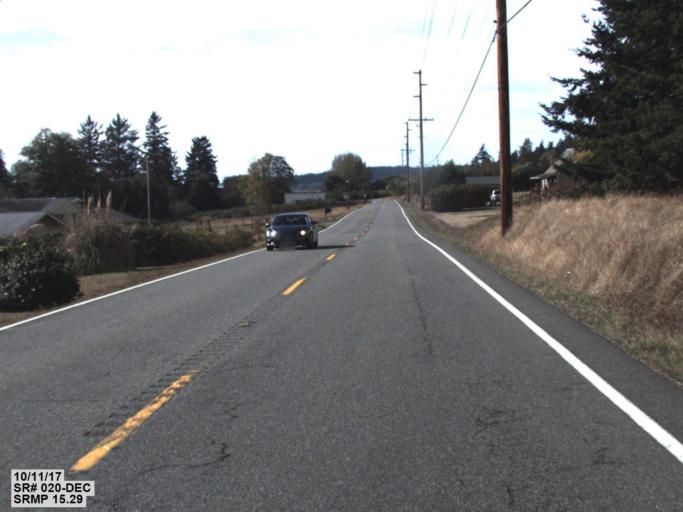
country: US
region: Washington
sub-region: Island County
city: Coupeville
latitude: 48.1709
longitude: -122.6312
